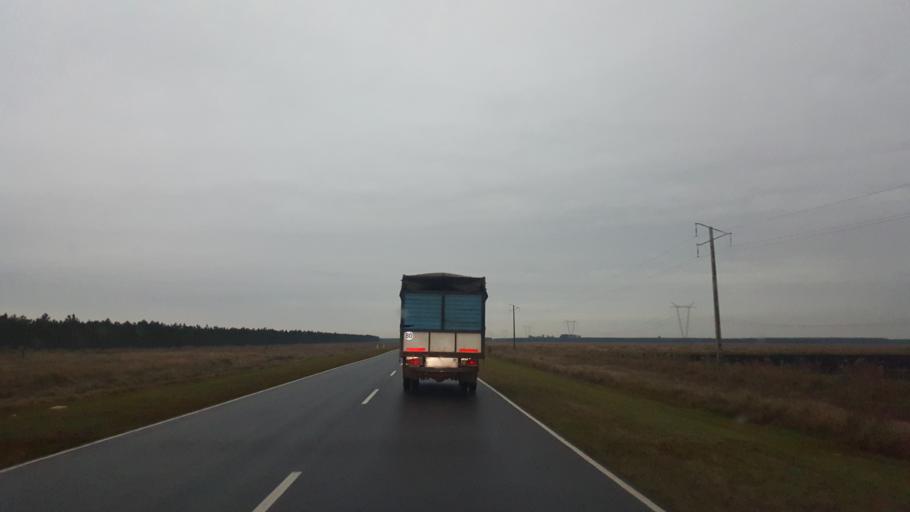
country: PY
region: Itapua
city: San Cosme y Damian
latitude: -27.5725
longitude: -56.2750
